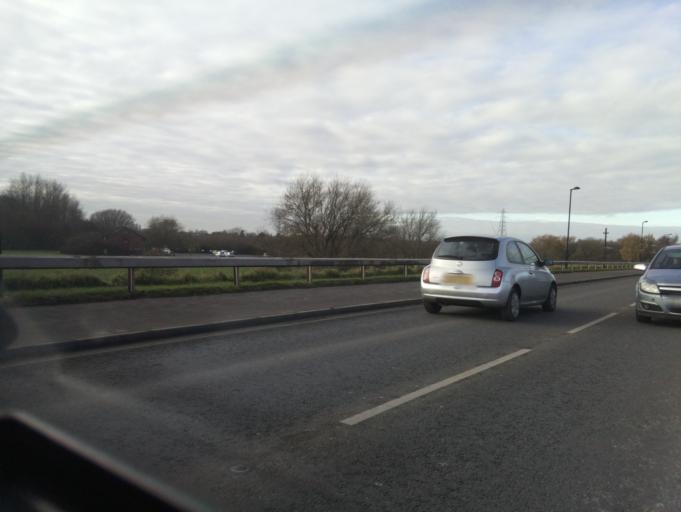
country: GB
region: England
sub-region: Staffordshire
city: Burton upon Trent
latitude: 52.7961
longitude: -1.6284
